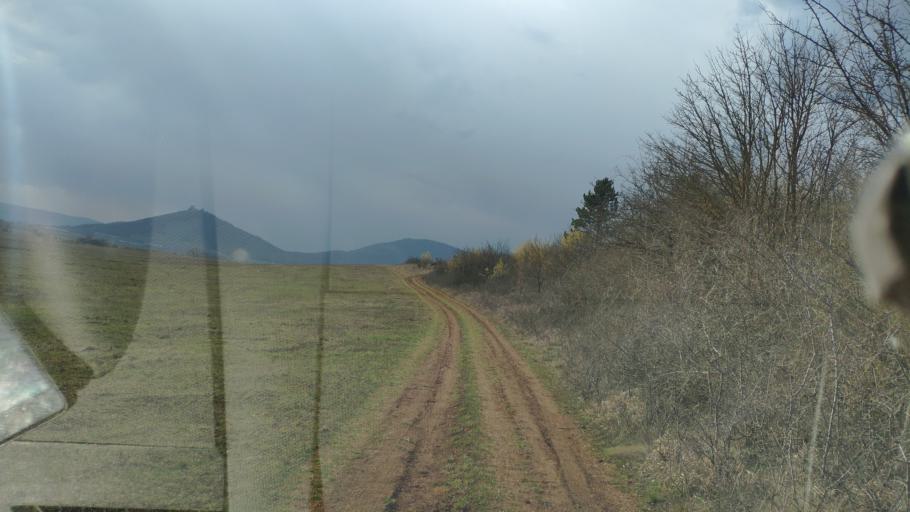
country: SK
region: Kosicky
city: Medzev
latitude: 48.6171
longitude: 20.9127
